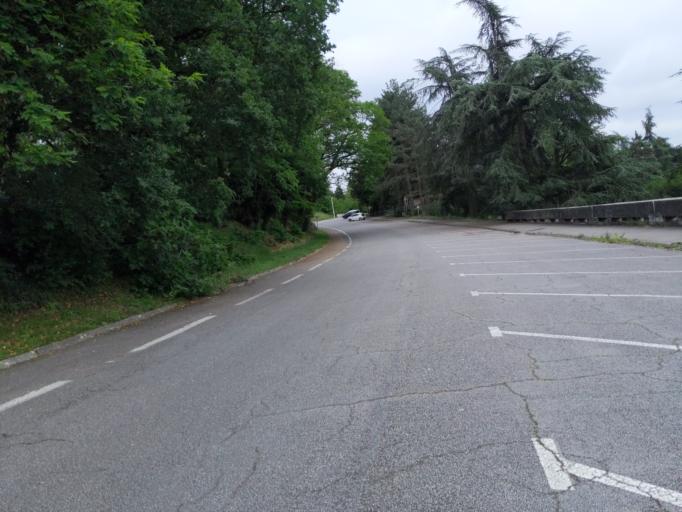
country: FR
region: Rhone-Alpes
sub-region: Departement du Rhone
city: Bron
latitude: 45.7274
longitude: 4.8921
